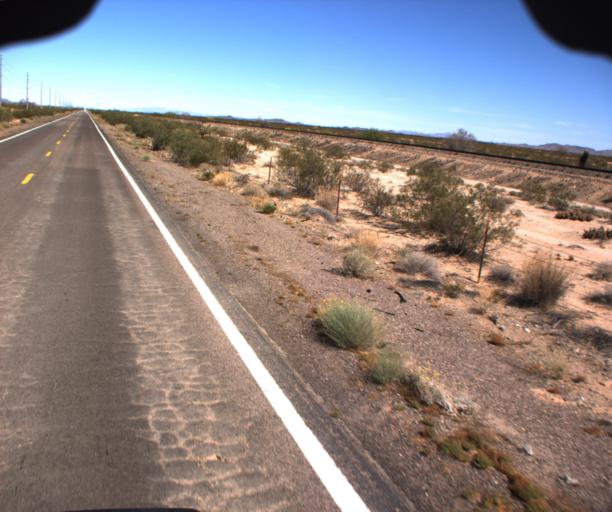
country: US
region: Arizona
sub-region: La Paz County
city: Salome
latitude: 33.8177
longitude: -113.8581
